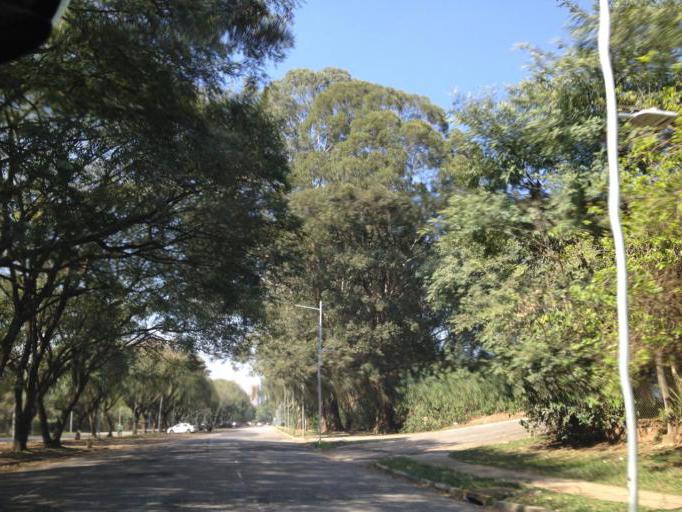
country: BR
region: Sao Paulo
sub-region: Osasco
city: Osasco
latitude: -23.5580
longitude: -46.7182
